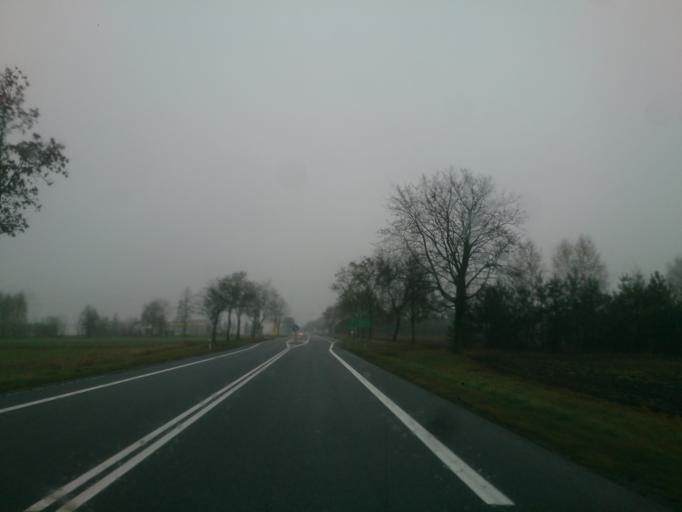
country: PL
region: Masovian Voivodeship
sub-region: Powiat sierpecki
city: Zawidz
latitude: 52.7971
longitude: 19.8641
